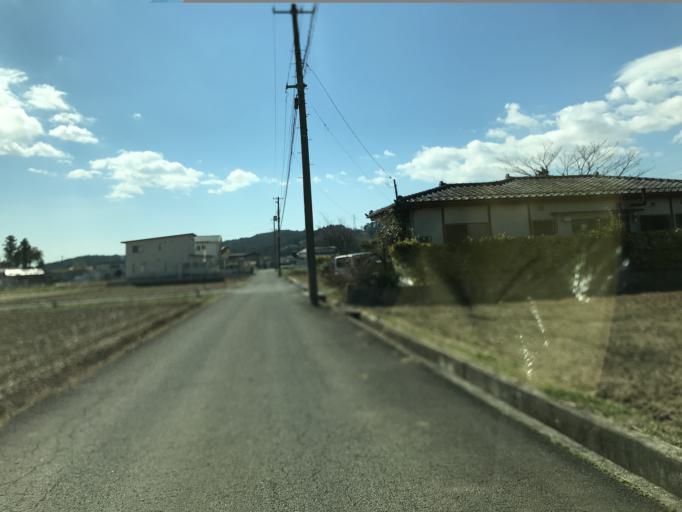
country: JP
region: Fukushima
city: Fukushima-shi
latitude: 37.7365
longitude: 140.4136
